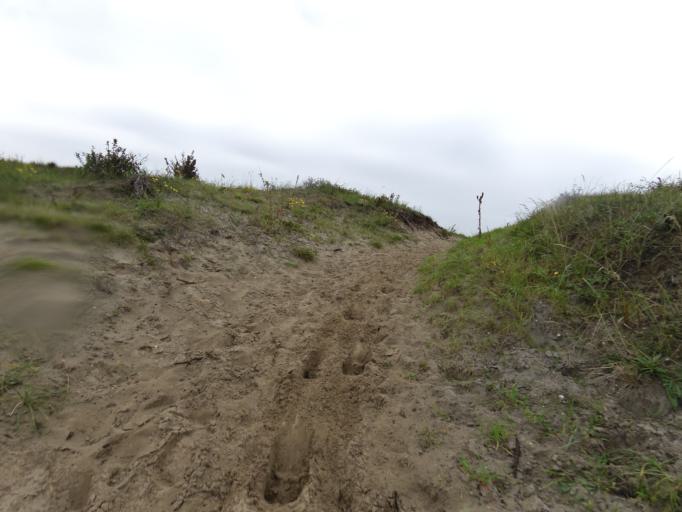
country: NL
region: South Holland
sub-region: Gemeente Hellevoetsluis
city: Nieuw-Helvoet
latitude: 51.8607
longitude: 4.0634
